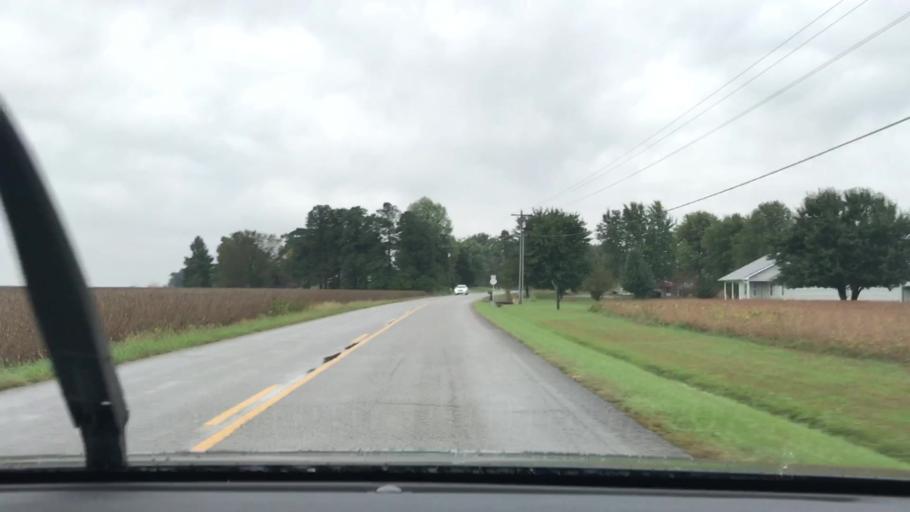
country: US
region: Kentucky
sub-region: McLean County
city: Calhoun
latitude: 37.4343
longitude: -87.2486
